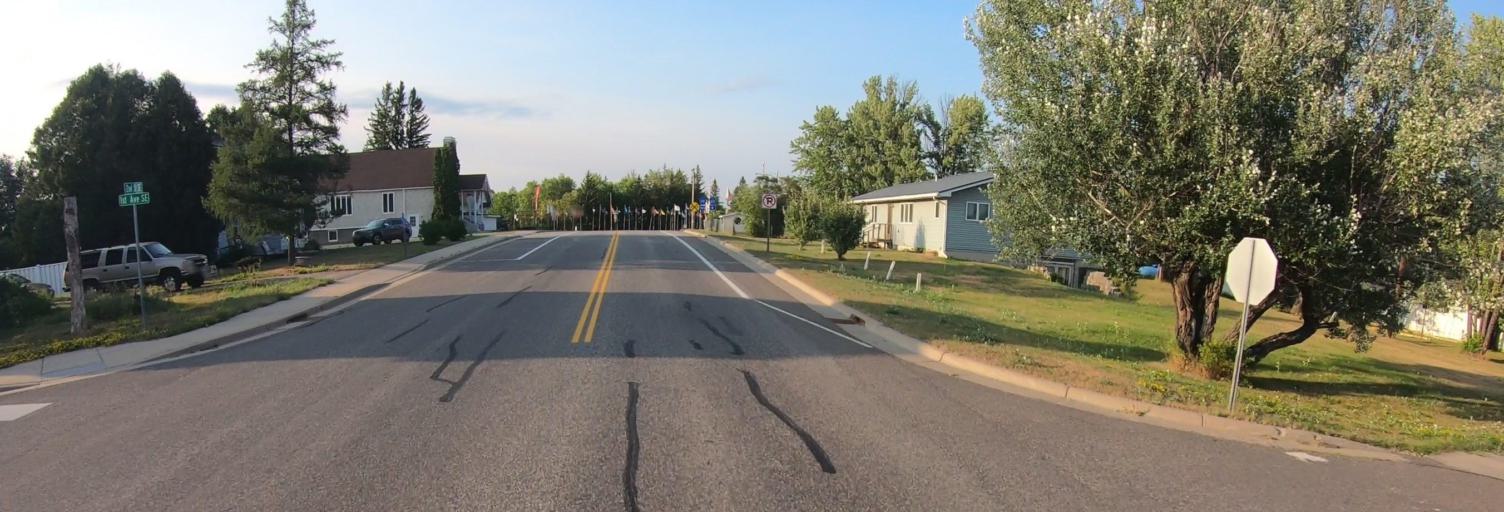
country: US
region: Minnesota
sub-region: Saint Louis County
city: Mountain Iron
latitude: 47.8520
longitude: -92.6822
